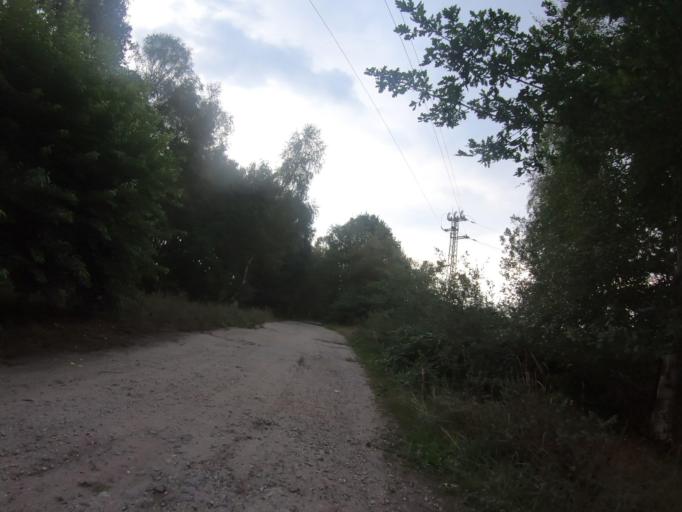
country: DE
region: Lower Saxony
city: Sassenburg
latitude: 52.5569
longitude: 10.6520
